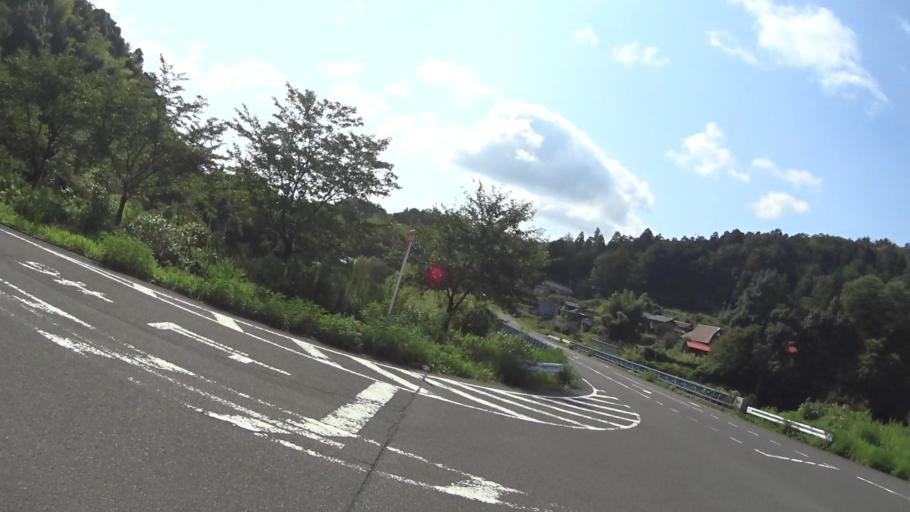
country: JP
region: Kyoto
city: Miyazu
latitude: 35.6326
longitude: 135.2127
